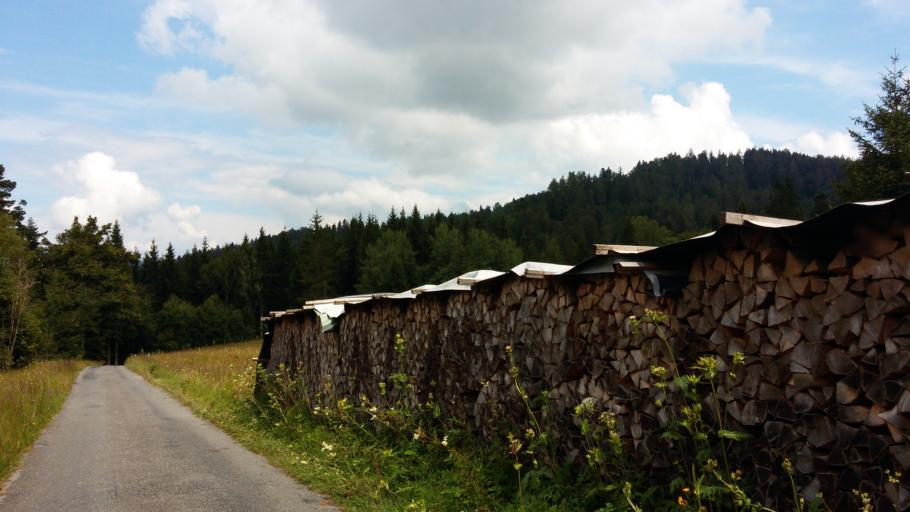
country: CH
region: Zug
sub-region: Zug
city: Unterageri
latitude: 47.1020
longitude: 8.5787
